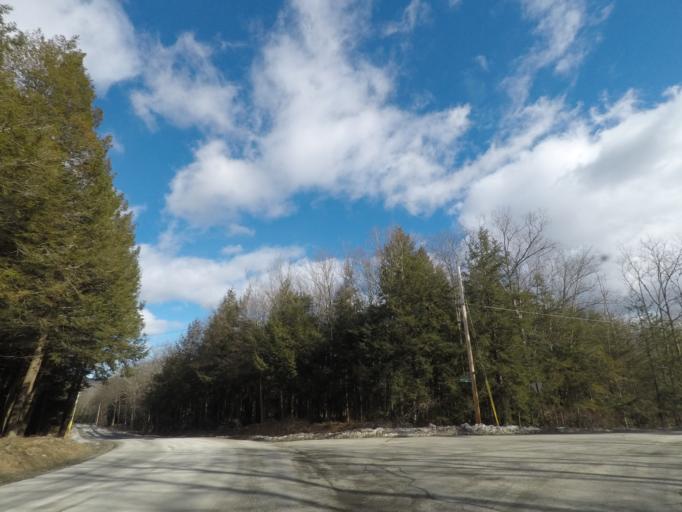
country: US
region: New York
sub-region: Rensselaer County
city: Averill Park
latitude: 42.6684
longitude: -73.5069
